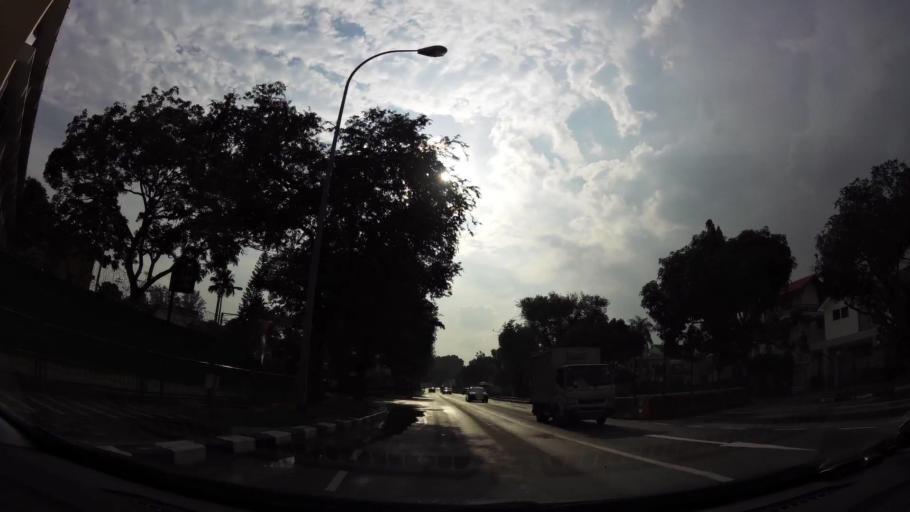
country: SG
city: Singapore
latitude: 1.3195
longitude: 103.9549
